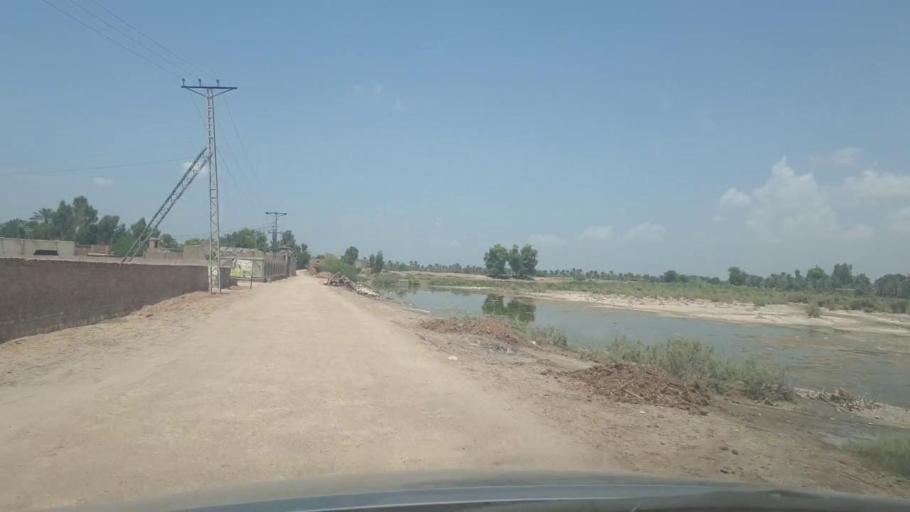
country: PK
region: Sindh
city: Kot Diji
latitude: 27.4197
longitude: 68.7368
